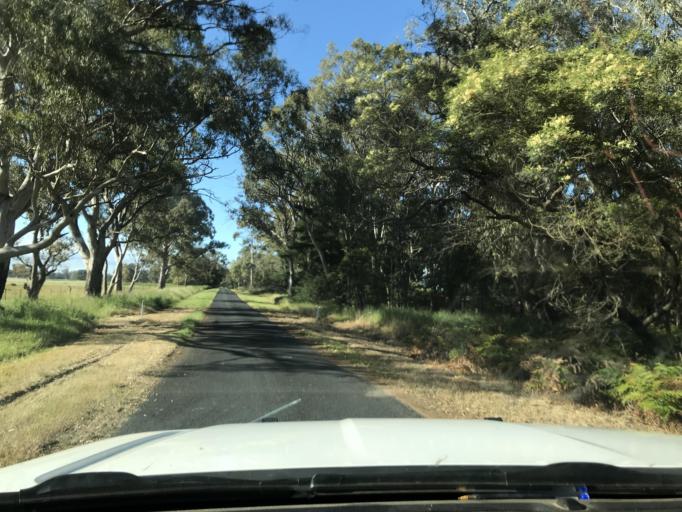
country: AU
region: South Australia
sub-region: Wattle Range
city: Penola
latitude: -37.2000
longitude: 140.9714
